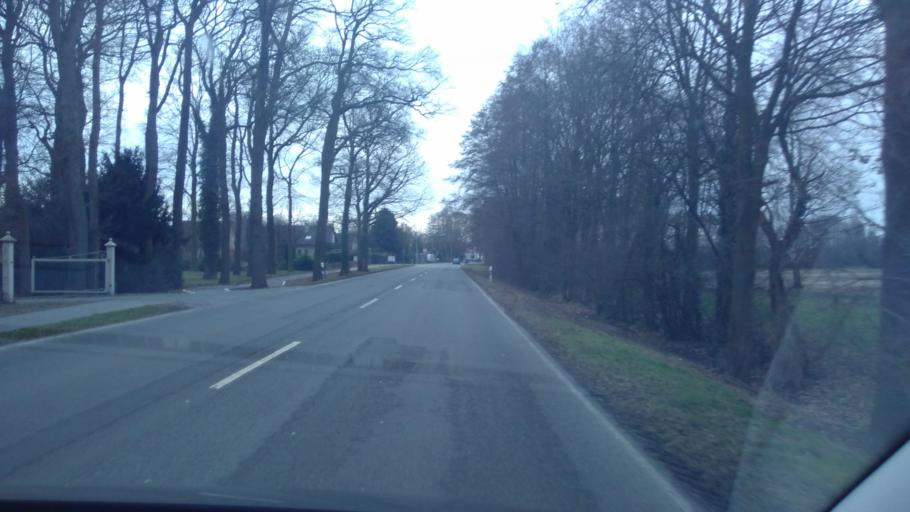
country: DE
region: North Rhine-Westphalia
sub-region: Regierungsbezirk Detmold
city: Delbruck
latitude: 51.8205
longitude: 8.5582
